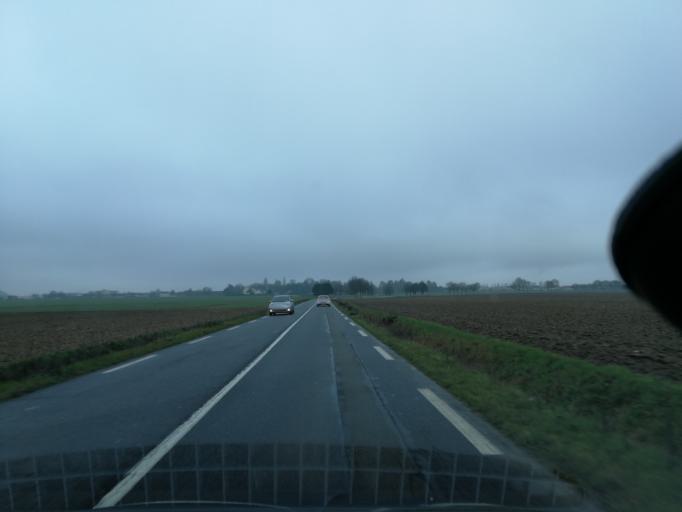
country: FR
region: Ile-de-France
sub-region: Departement de l'Essonne
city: Villiers-le-Bacle
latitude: 48.7375
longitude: 2.1076
